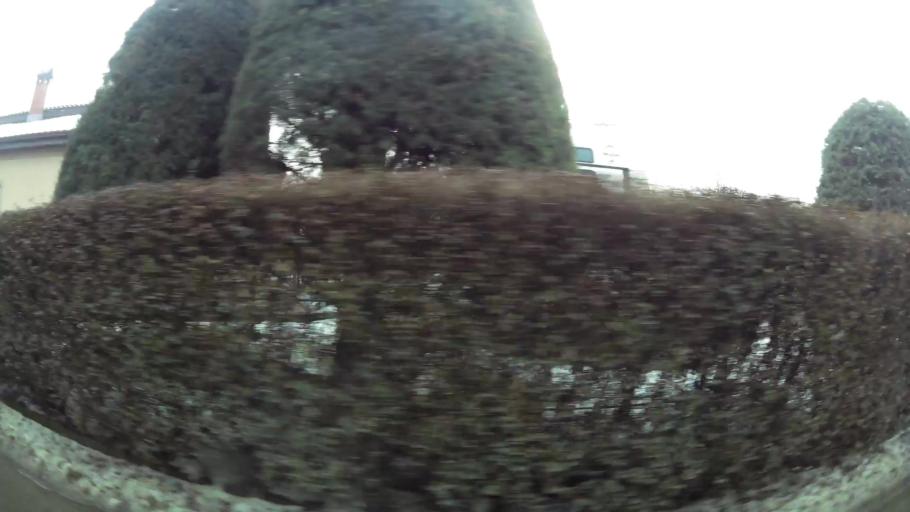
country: MK
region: Ilinden
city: Jurumleri
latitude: 41.9678
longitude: 21.5569
